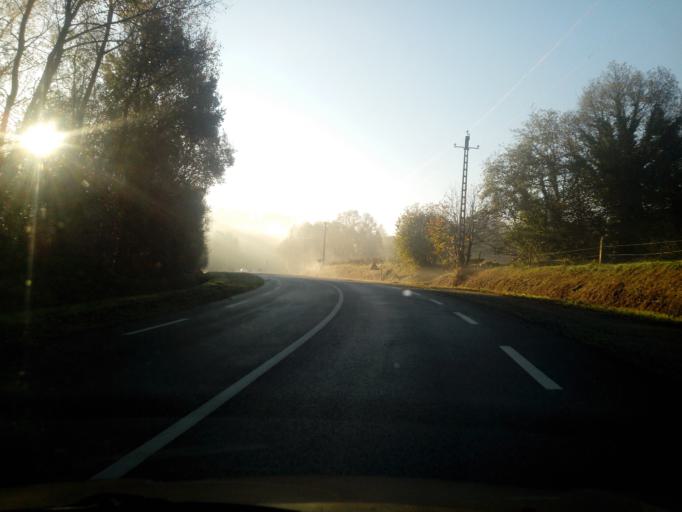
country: FR
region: Brittany
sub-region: Departement du Morbihan
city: Pluherlin
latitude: 47.7084
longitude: -2.3376
